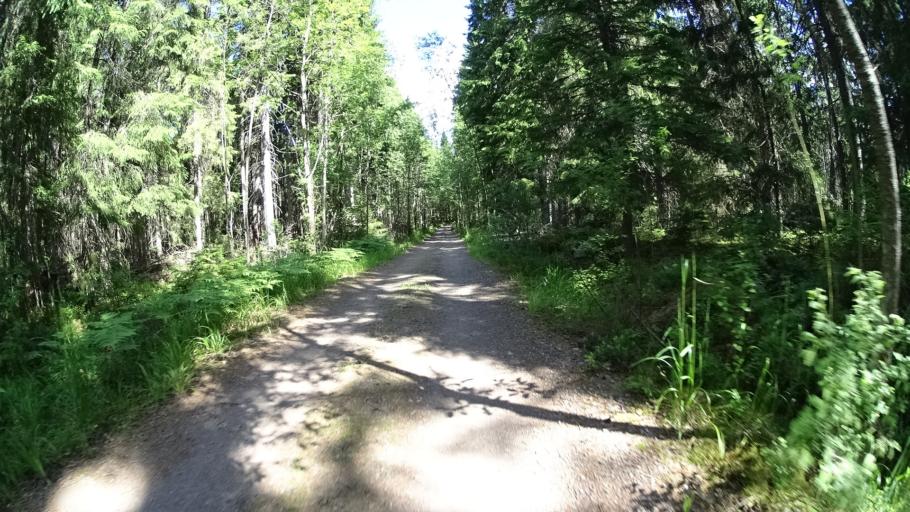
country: FI
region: Uusimaa
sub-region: Helsinki
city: Vihti
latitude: 60.3199
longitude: 24.4482
